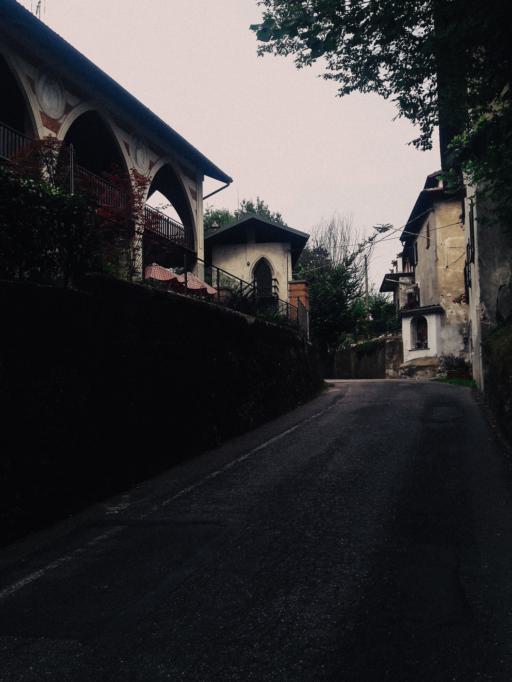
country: IT
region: Lombardy
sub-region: Provincia di Varese
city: Castiglione Olona
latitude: 45.7558
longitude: 8.8683
